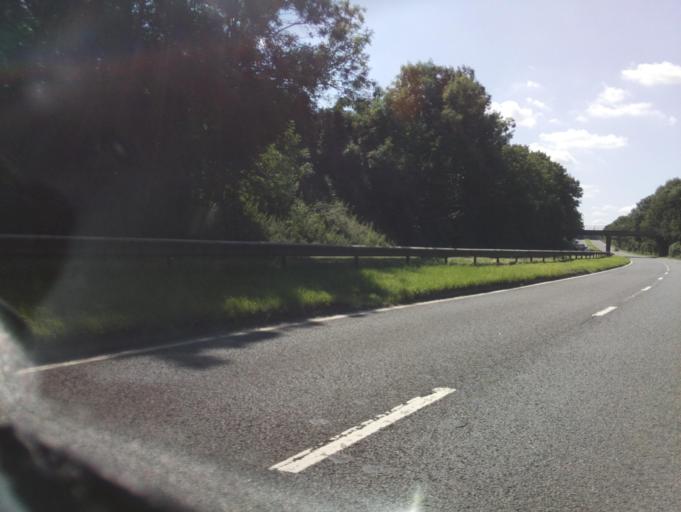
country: GB
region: England
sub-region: Warwickshire
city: Atherstone
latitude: 52.5808
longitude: -1.5450
